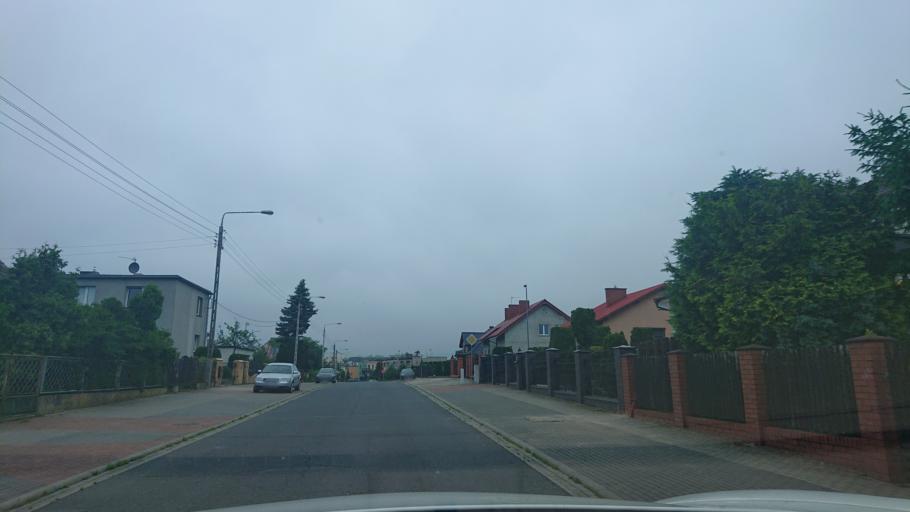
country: PL
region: Greater Poland Voivodeship
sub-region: Powiat gnieznienski
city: Gniezno
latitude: 52.5107
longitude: 17.6002
